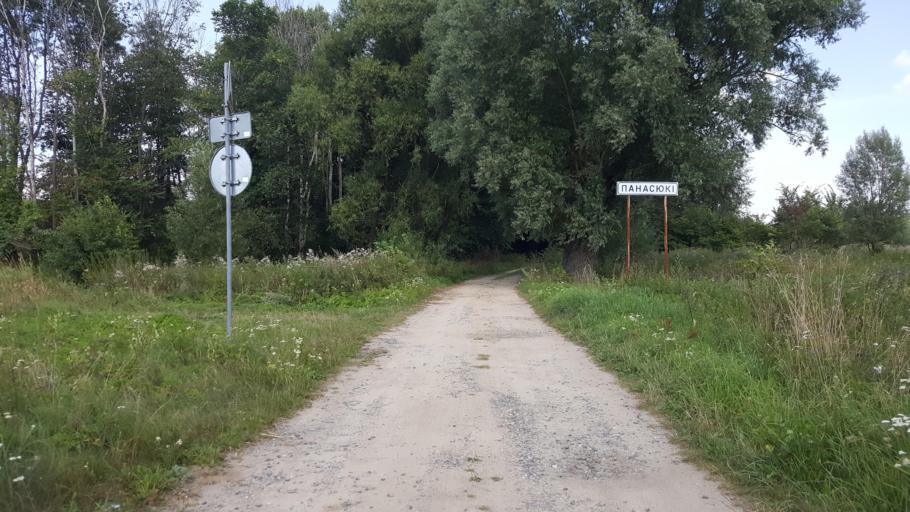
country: PL
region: Podlasie
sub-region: Powiat hajnowski
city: Hajnowka
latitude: 52.5652
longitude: 23.6119
